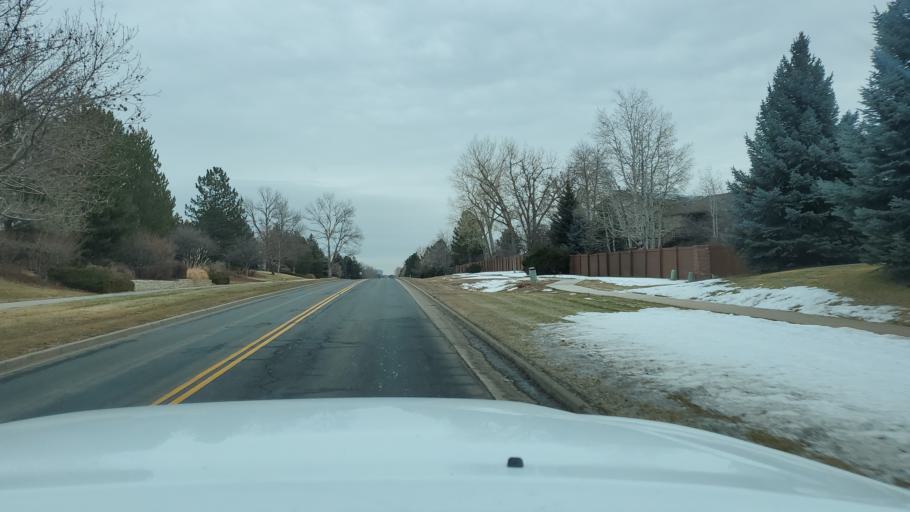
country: US
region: Colorado
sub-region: Arapahoe County
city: Greenwood Village
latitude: 39.6096
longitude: -104.9326
